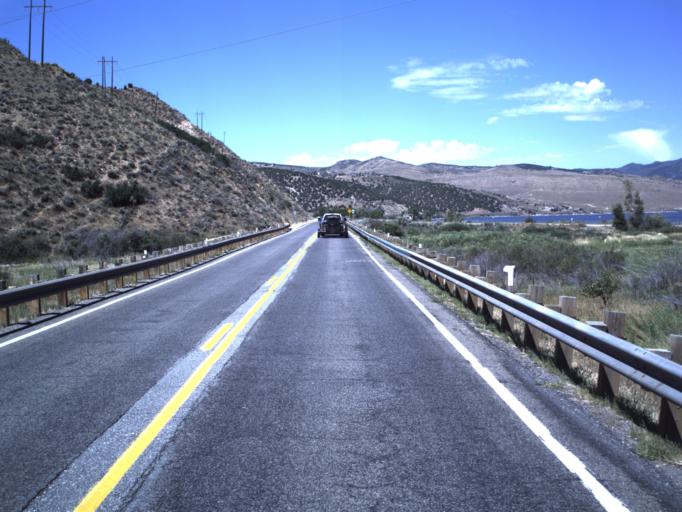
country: US
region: Utah
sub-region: Summit County
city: Oakley
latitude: 40.7520
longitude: -111.3734
